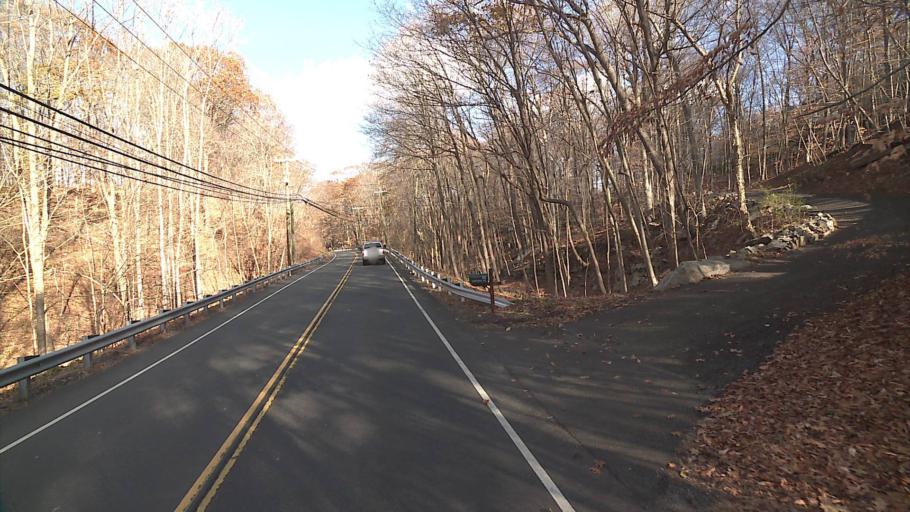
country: US
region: Connecticut
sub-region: Fairfield County
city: Georgetown
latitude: 41.2391
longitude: -73.3813
